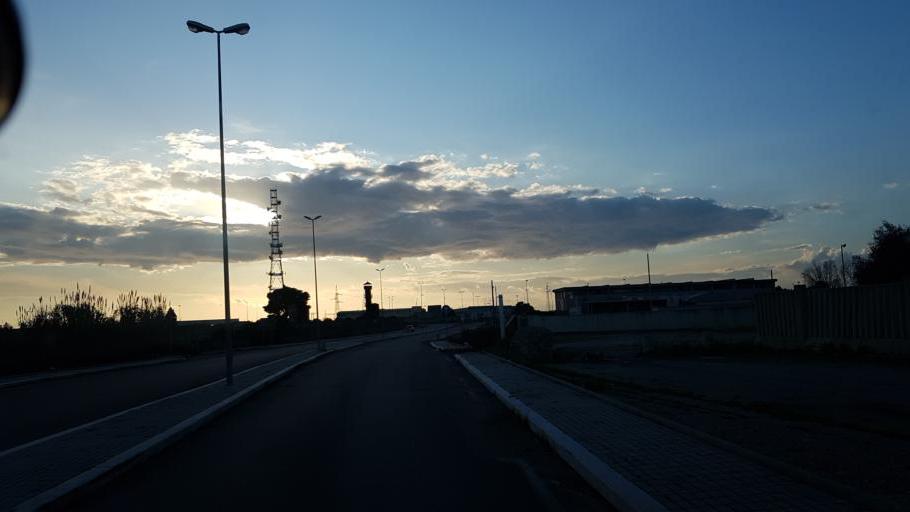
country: IT
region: Apulia
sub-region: Provincia di Lecce
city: Surbo
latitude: 40.3880
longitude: 18.1189
